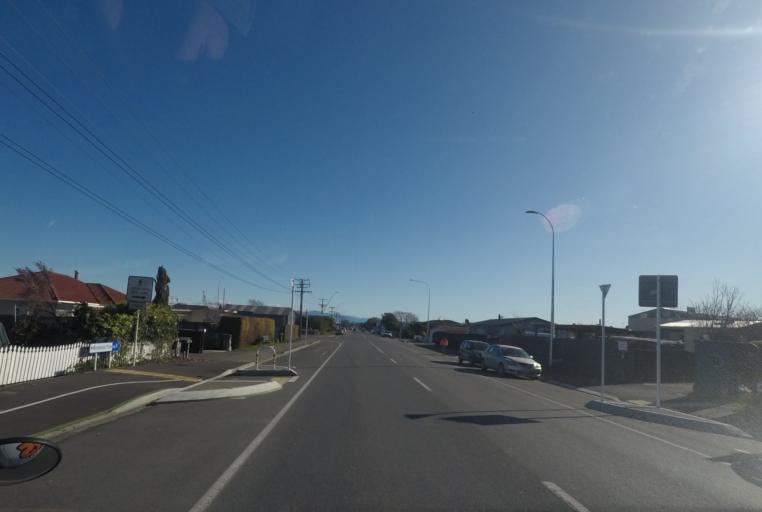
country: NZ
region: Nelson
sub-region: Nelson City
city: Nelson
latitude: -41.2920
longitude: 173.2454
